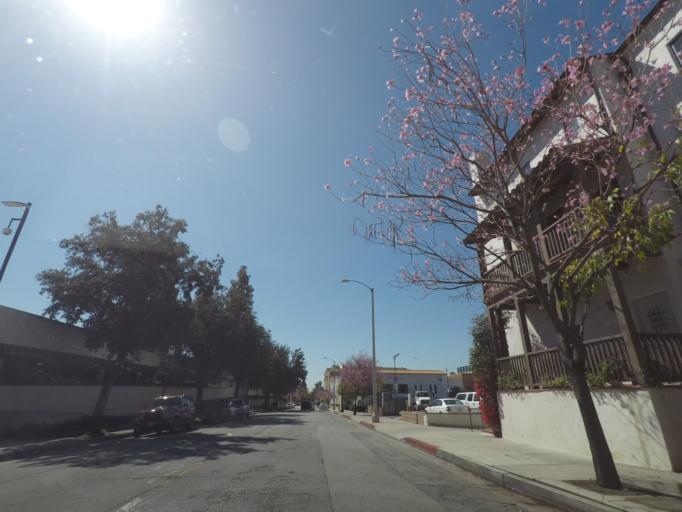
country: US
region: California
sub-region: Los Angeles County
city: Pasadena
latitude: 34.1474
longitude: -118.1353
